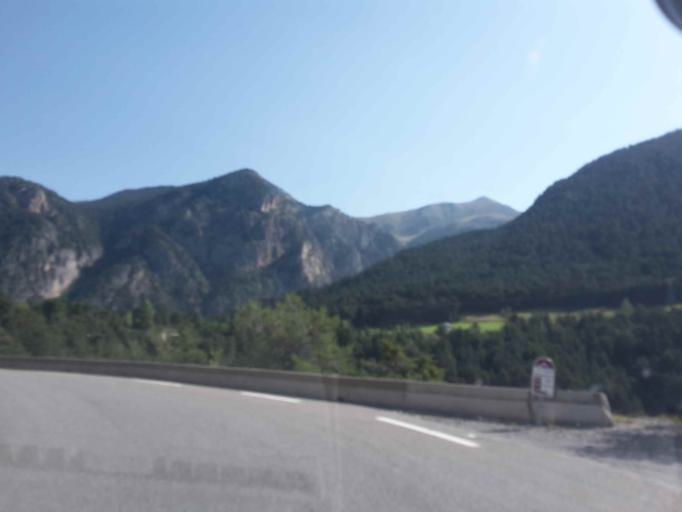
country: FR
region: Provence-Alpes-Cote d'Azur
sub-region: Departement des Hautes-Alpes
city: Guillestre
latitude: 44.6330
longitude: 6.6717
